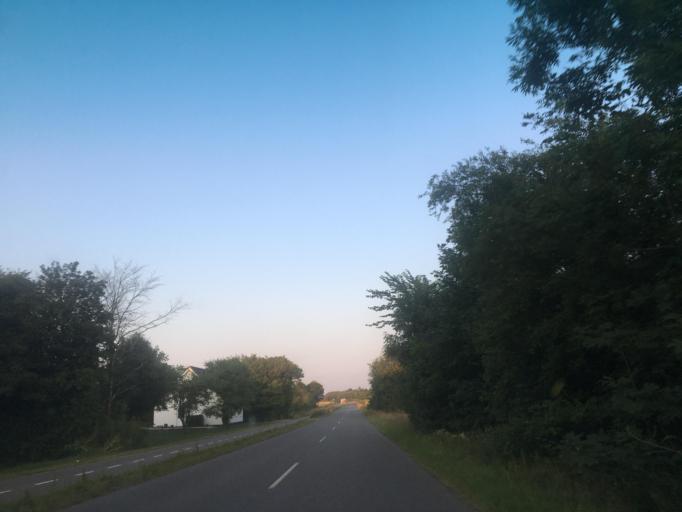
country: DK
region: North Denmark
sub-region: Thisted Kommune
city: Hurup
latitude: 56.7533
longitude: 8.3832
